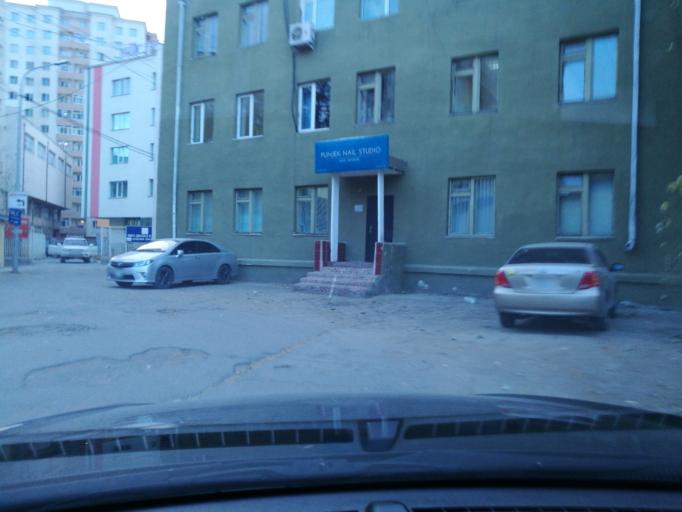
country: MN
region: Ulaanbaatar
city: Ulaanbaatar
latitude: 47.9241
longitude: 106.9216
